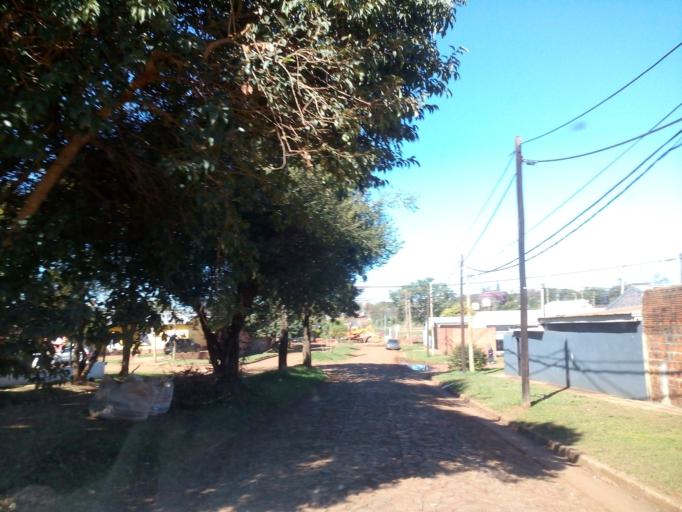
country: AR
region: Misiones
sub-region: Departamento de Capital
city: Posadas
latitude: -27.3889
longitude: -55.9405
